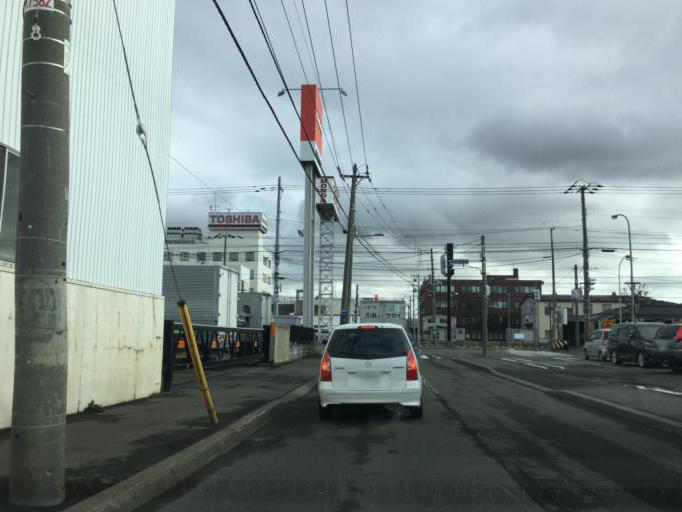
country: JP
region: Hokkaido
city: Sapporo
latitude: 43.0283
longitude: 141.4412
